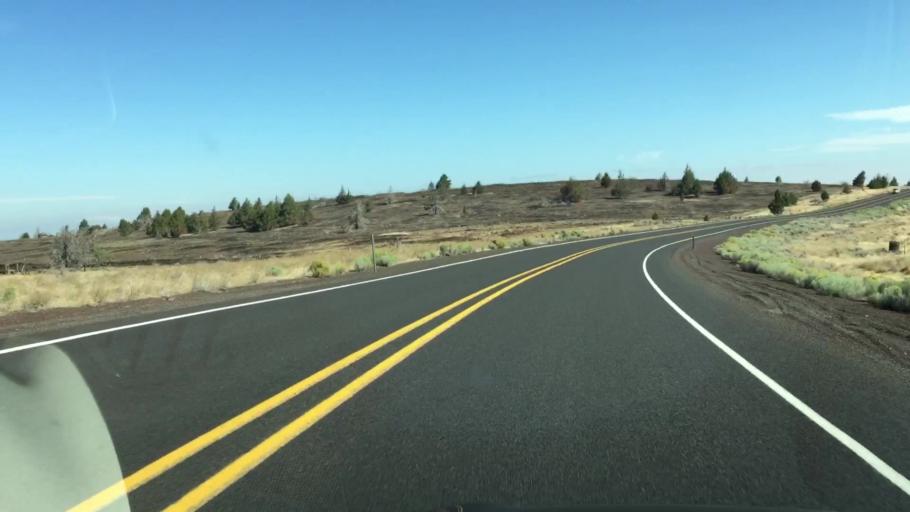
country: US
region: Oregon
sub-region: Jefferson County
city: Warm Springs
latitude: 45.0045
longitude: -120.9957
